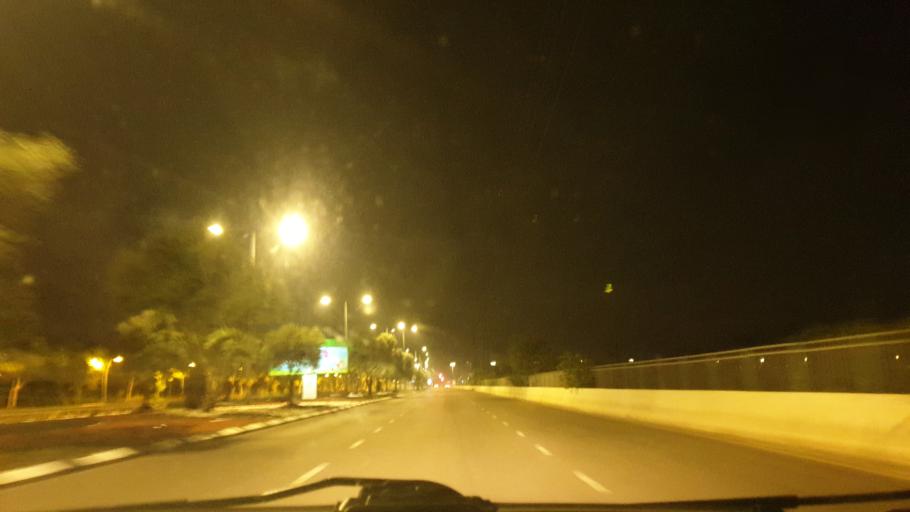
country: IL
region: Central District
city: Kefar Habad
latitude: 31.9720
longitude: 34.8358
